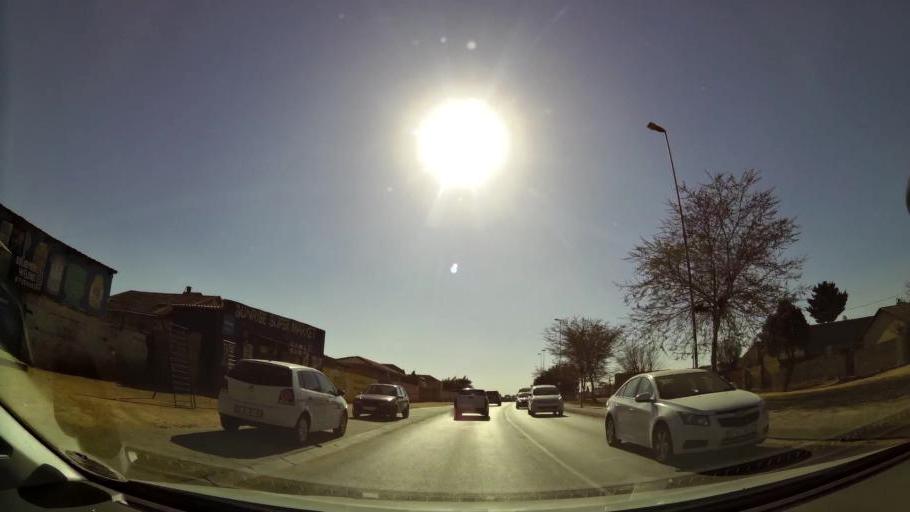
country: ZA
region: Gauteng
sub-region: Ekurhuleni Metropolitan Municipality
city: Tembisa
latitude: -26.0244
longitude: 28.2301
